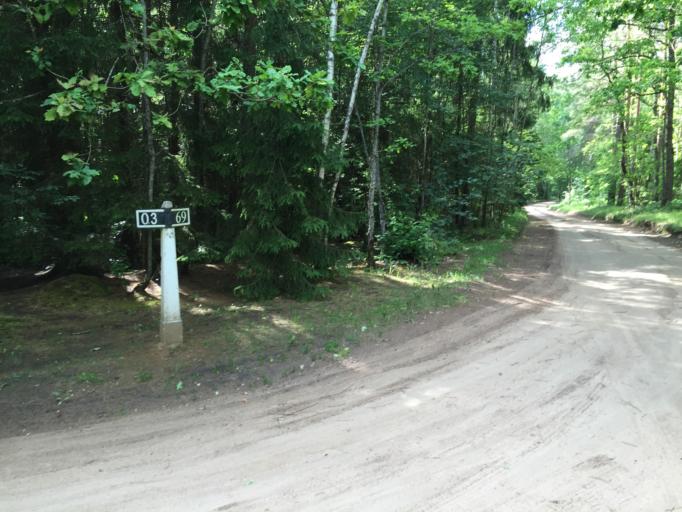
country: LV
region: Vecumnieki
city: Vecumnieki
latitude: 56.4415
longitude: 24.5840
